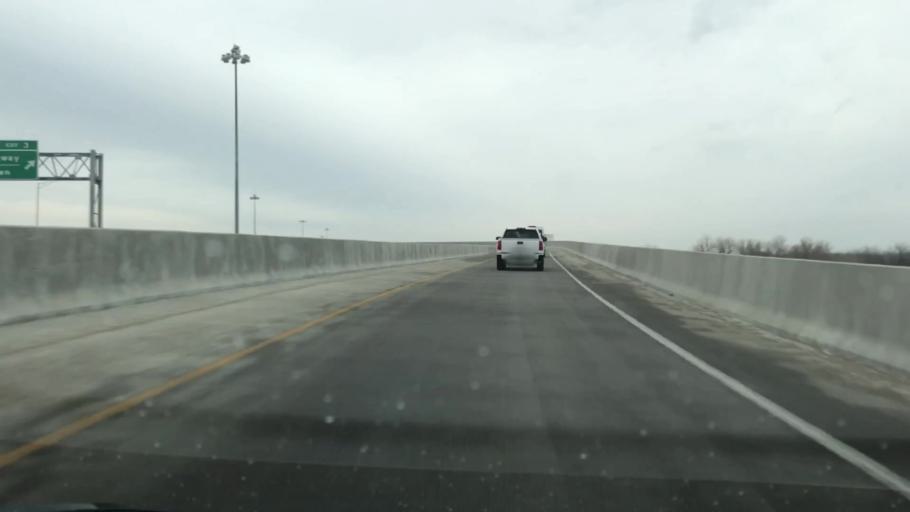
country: US
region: Iowa
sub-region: Pottawattamie County
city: Council Bluffs
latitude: 41.2325
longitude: -95.8305
